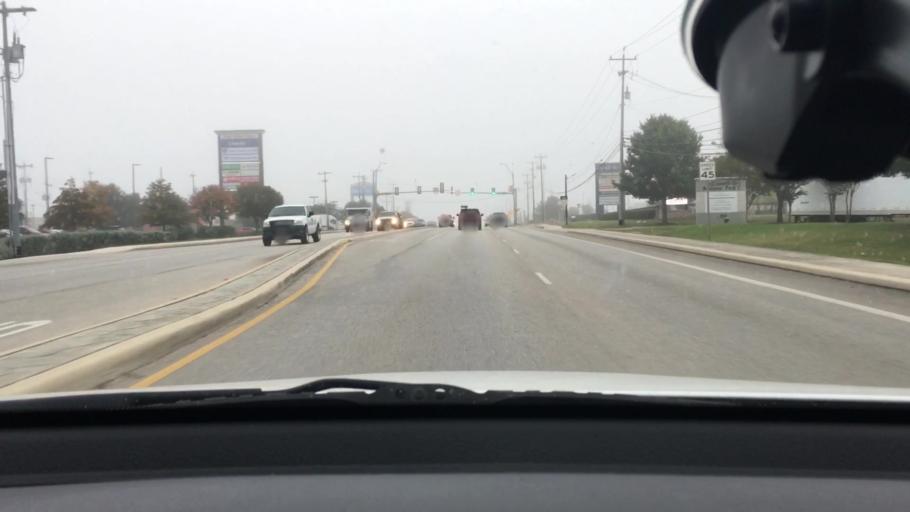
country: US
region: Texas
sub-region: Bexar County
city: Selma
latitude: 29.6046
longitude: -98.2798
